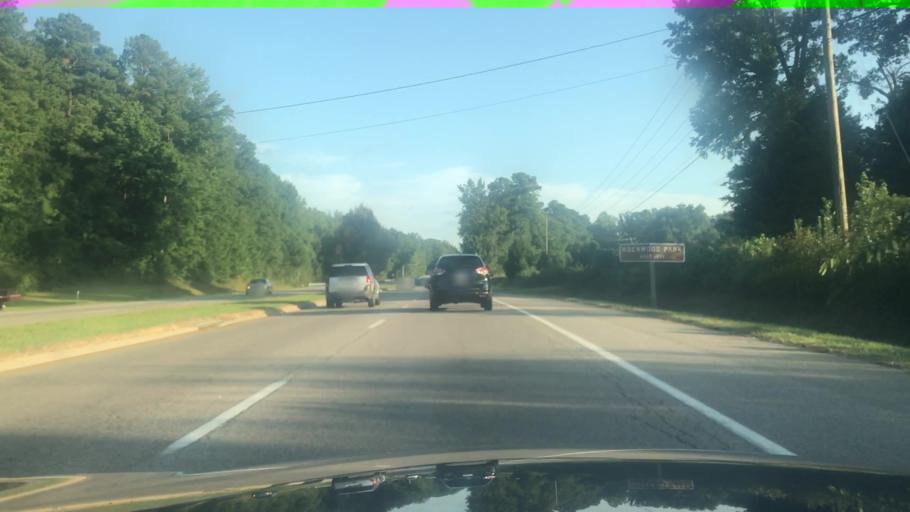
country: US
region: Virginia
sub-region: Chesterfield County
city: Brandermill
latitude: 37.4515
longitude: -77.5861
